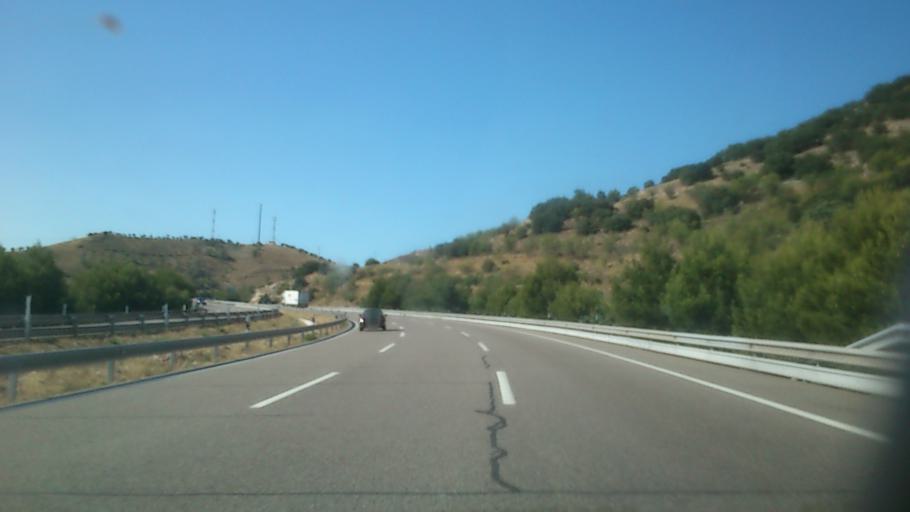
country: ES
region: Aragon
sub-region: Provincia de Zaragoza
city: Paracuellos de la Ribera
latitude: 41.4054
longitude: -1.5256
